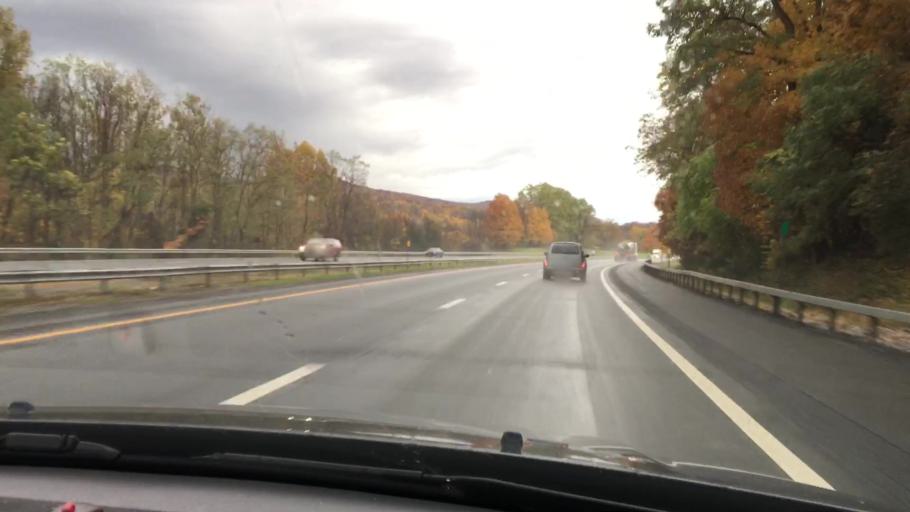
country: US
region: New York
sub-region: Orange County
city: Firthcliffe
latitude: 41.4160
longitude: -74.0705
